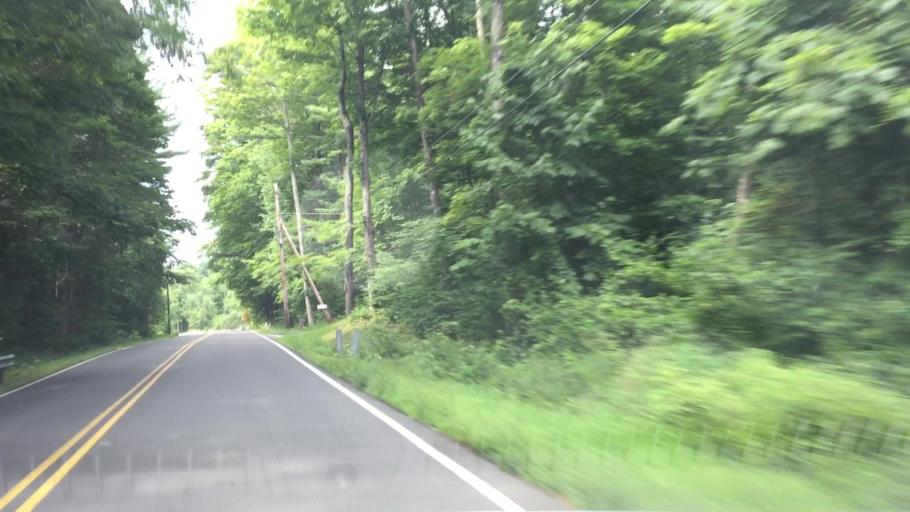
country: US
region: Massachusetts
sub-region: Berkshire County
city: Housatonic
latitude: 42.2239
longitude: -73.4062
